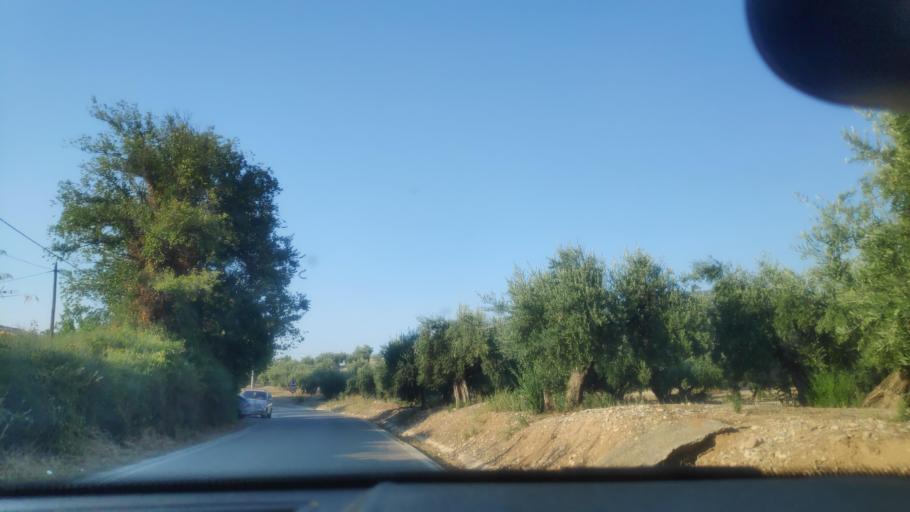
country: ES
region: Andalusia
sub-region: Provincia de Jaen
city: Jaen
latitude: 37.7210
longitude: -3.7610
